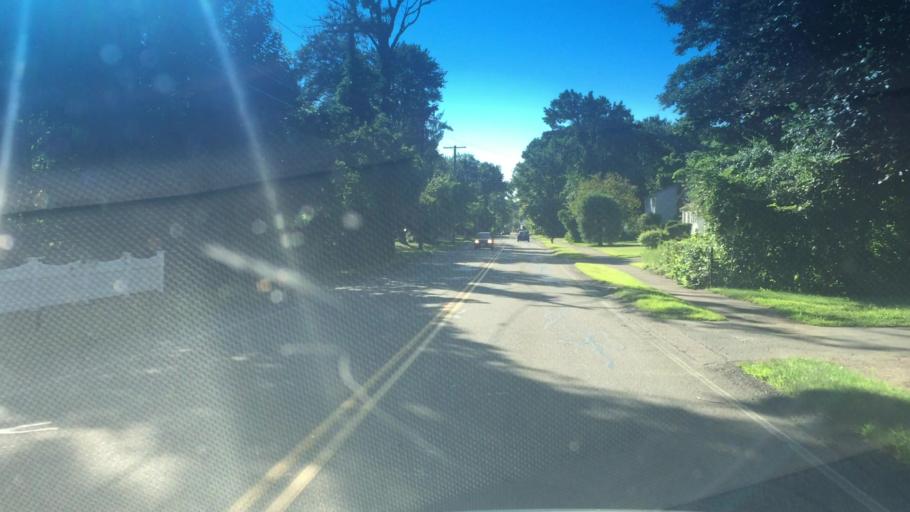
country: US
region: Massachusetts
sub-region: Norfolk County
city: Norwood
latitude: 42.1609
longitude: -71.2081
